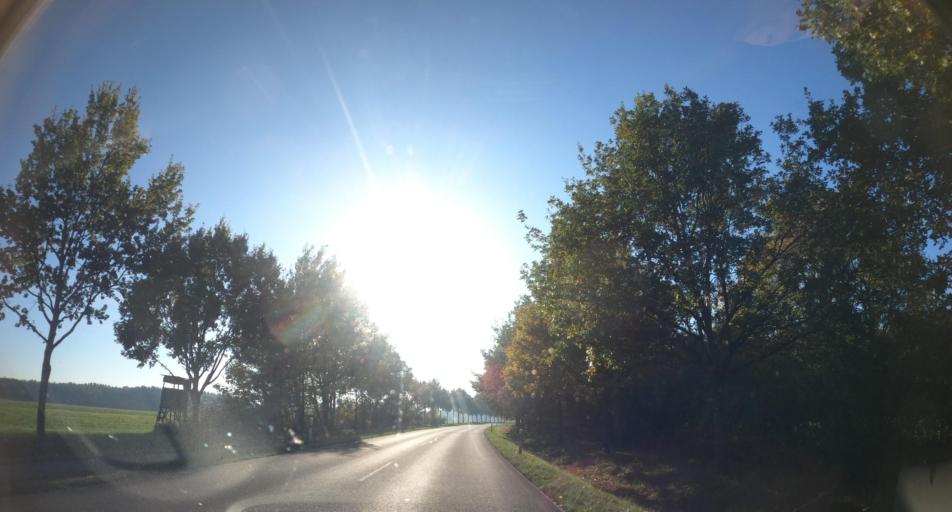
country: DE
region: Mecklenburg-Vorpommern
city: Ueckermunde
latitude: 53.7295
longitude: 14.0904
